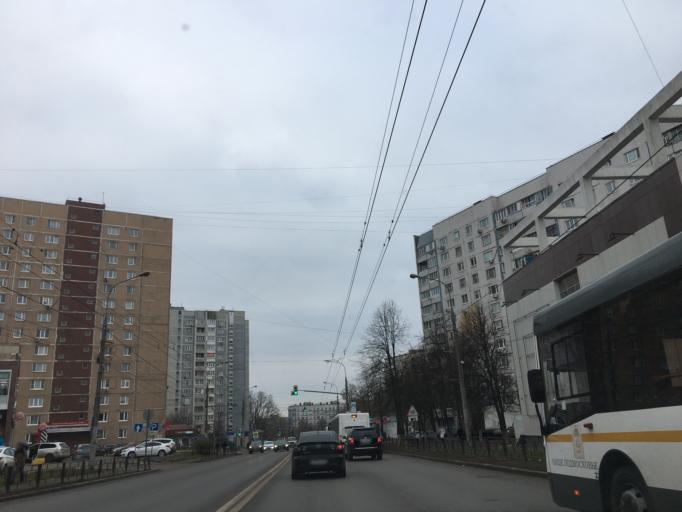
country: RU
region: Moskovskaya
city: Vidnoye
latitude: 55.5468
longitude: 37.7105
